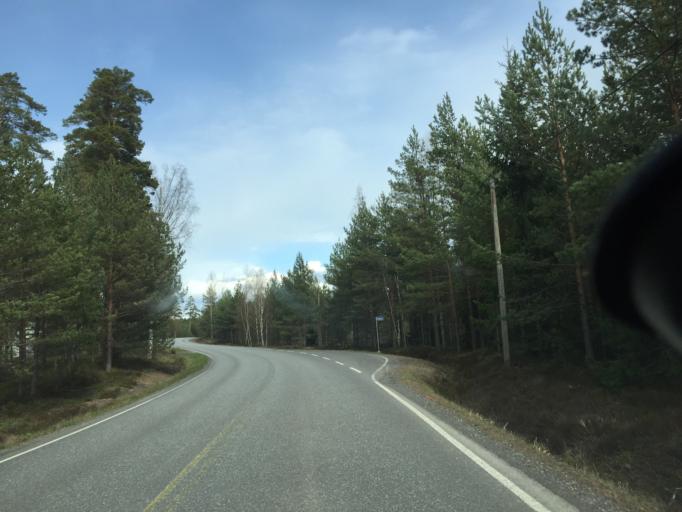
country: FI
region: Varsinais-Suomi
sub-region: Salo
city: Saerkisalo
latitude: 59.9978
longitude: 23.0782
